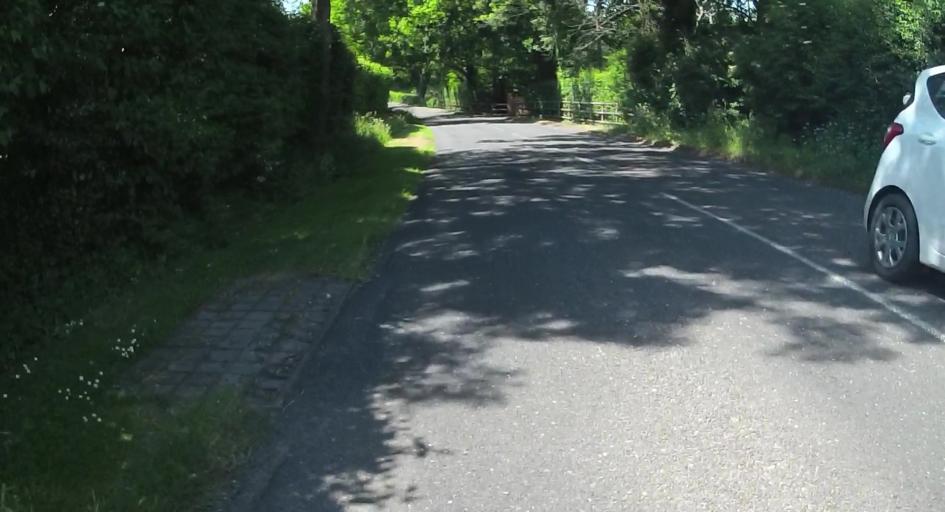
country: GB
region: England
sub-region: Hampshire
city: Kingsclere
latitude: 51.3631
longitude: -1.2316
